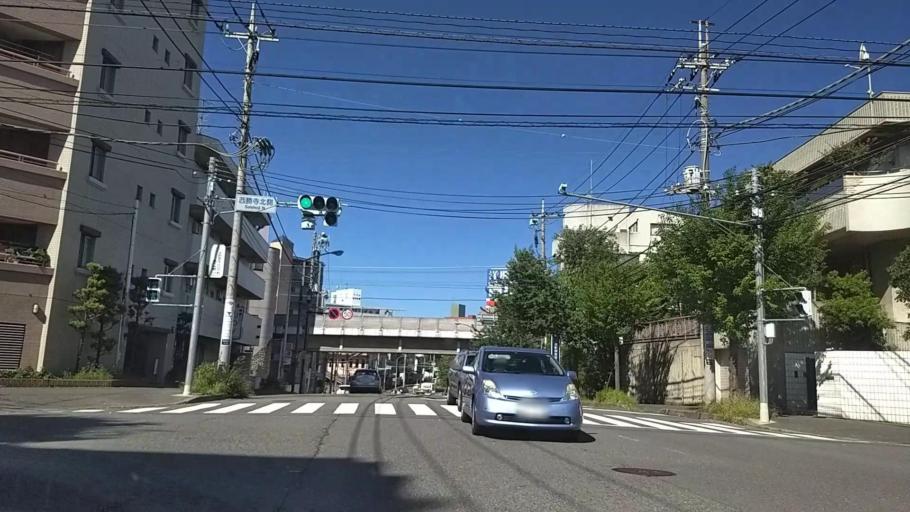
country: JP
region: Tokyo
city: Chofugaoka
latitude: 35.5711
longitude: 139.5547
